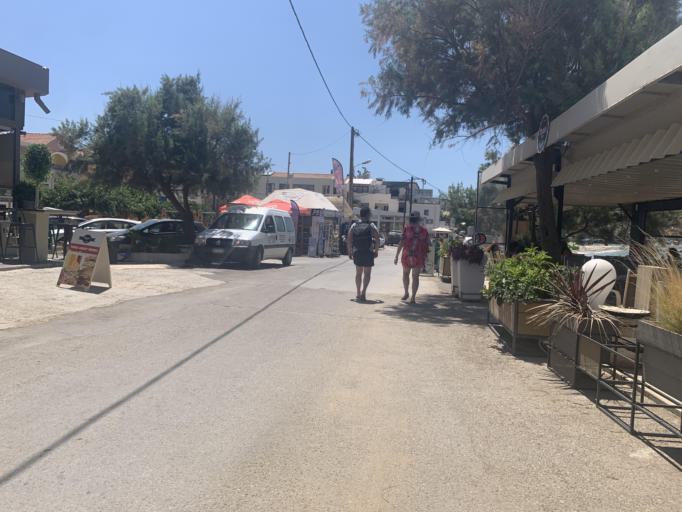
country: GR
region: Crete
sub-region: Nomos Chanias
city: Kalivai
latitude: 35.4492
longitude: 24.2026
